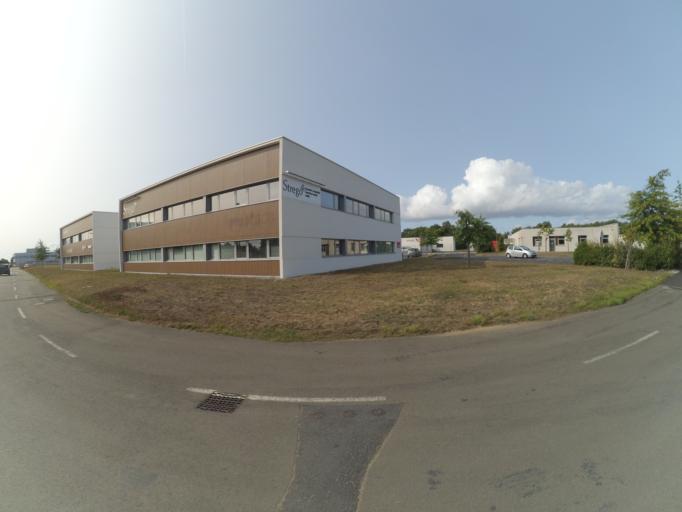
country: FR
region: Pays de la Loire
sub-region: Departement de la Vendee
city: Bouffere
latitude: 46.9754
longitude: -1.3354
